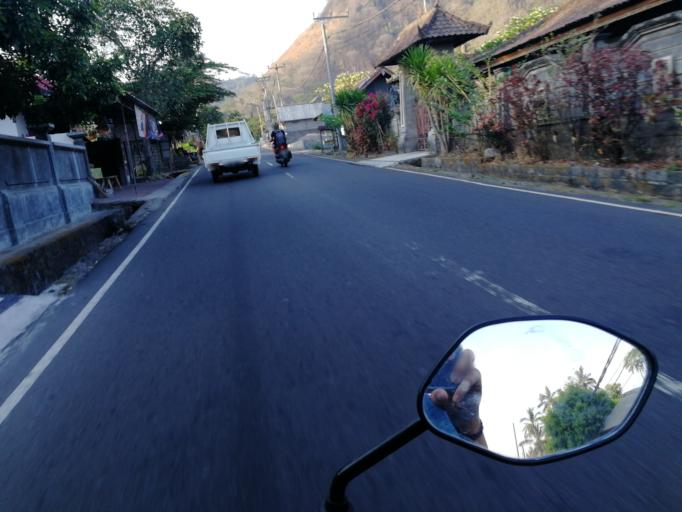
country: ID
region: Bali
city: Banjar Kangkaang
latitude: -8.3566
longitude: 115.6122
